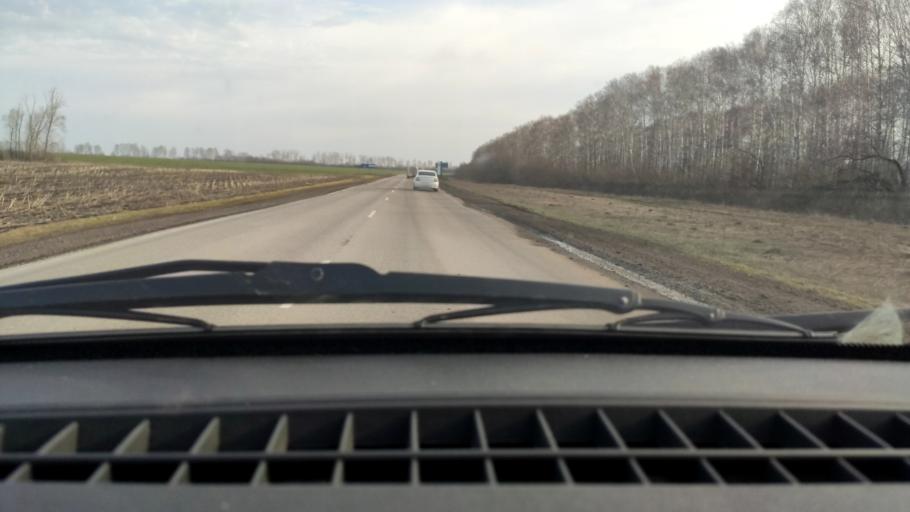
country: RU
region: Bashkortostan
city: Chishmy
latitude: 54.4903
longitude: 55.2749
